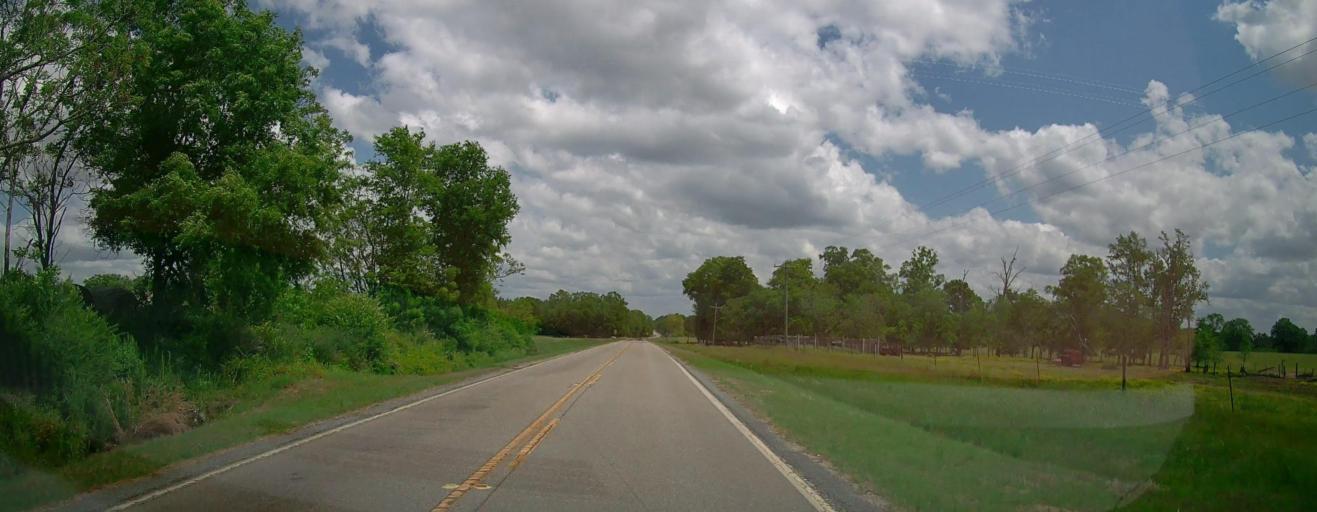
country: US
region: Georgia
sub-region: Dodge County
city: Chester
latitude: 32.5213
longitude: -83.2156
